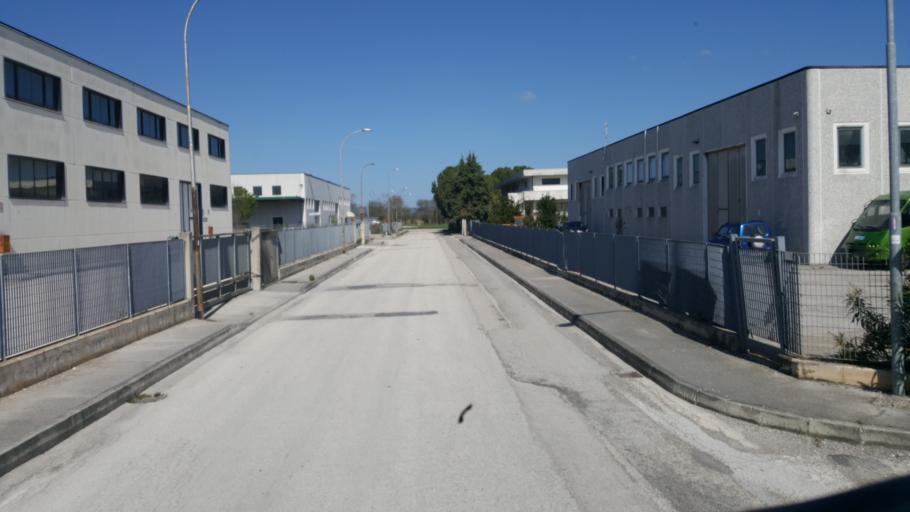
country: IT
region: The Marches
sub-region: Provincia di Macerata
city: Montecassiano
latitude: 43.3555
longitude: 13.4610
